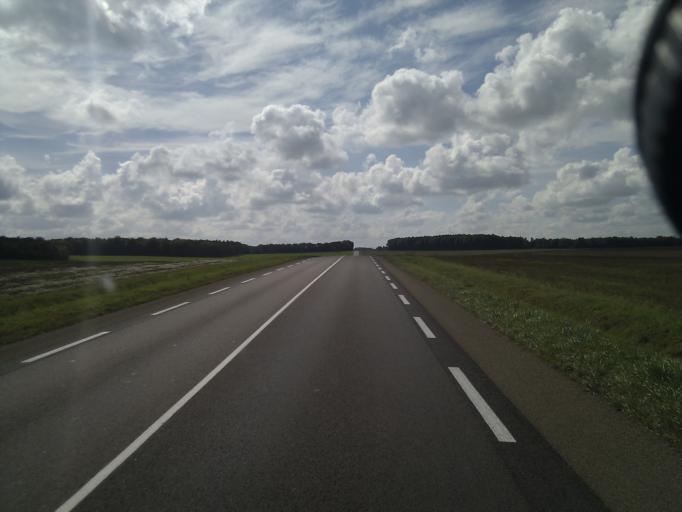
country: FR
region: Bourgogne
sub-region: Departement de la Cote-d'Or
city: Chatillon-sur-Seine
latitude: 47.7803
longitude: 4.5090
